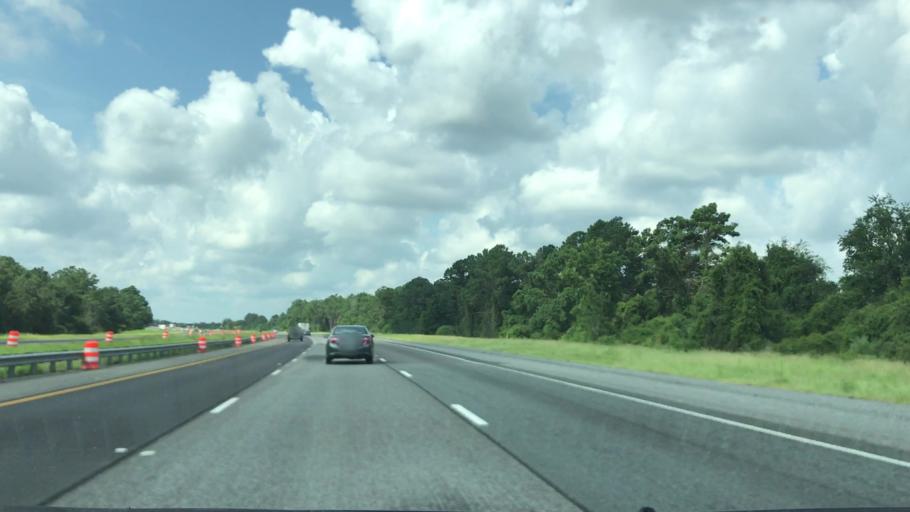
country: US
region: Georgia
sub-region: Camden County
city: Woodbine
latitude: 31.0464
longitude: -81.6497
